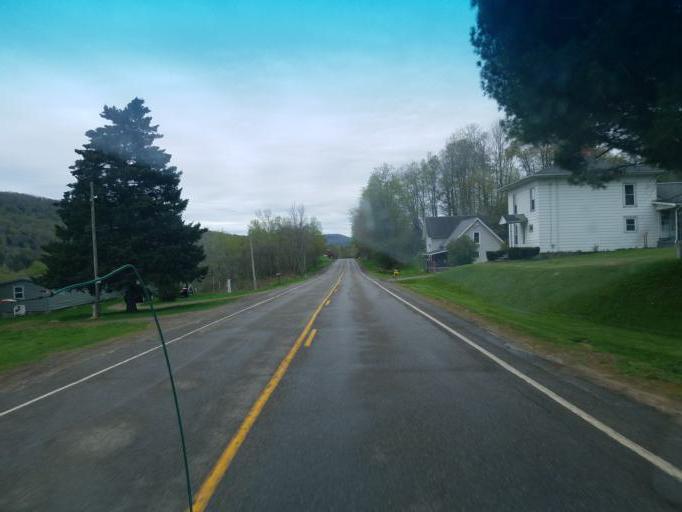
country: US
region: New York
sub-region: Allegany County
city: Wellsville
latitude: 42.0092
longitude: -77.8437
